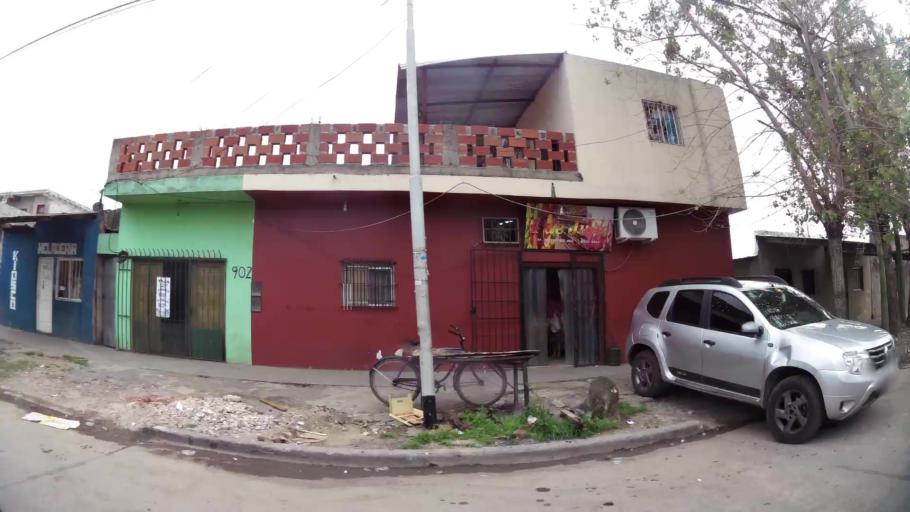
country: AR
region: Buenos Aires
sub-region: Partido de Avellaneda
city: Avellaneda
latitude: -34.6518
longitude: -58.3605
